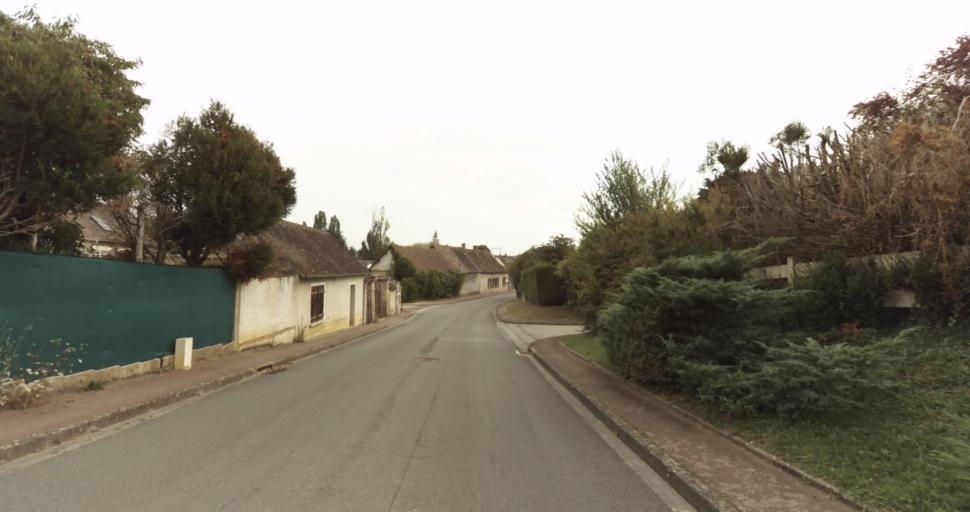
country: FR
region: Haute-Normandie
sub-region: Departement de l'Eure
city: Croth
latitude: 48.8726
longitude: 1.3587
